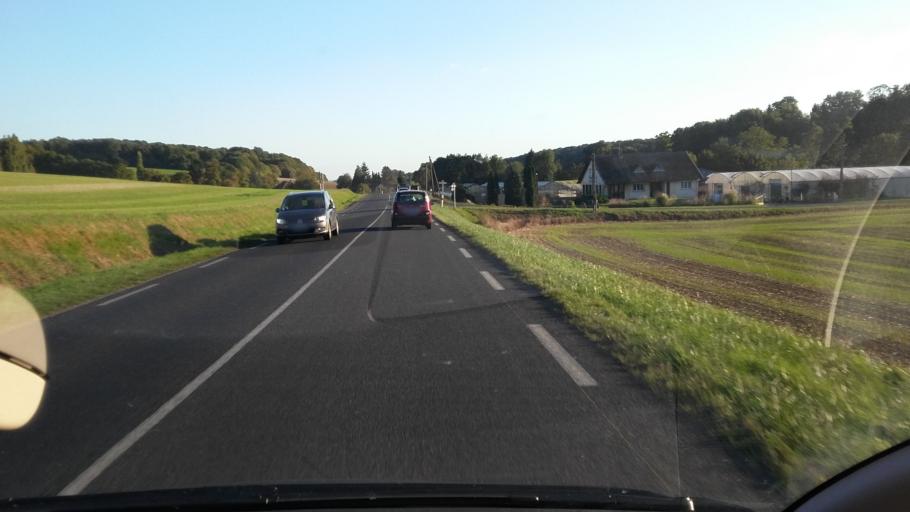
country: FR
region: Champagne-Ardenne
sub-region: Departement de la Marne
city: Verzenay
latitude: 49.1244
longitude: 4.1085
